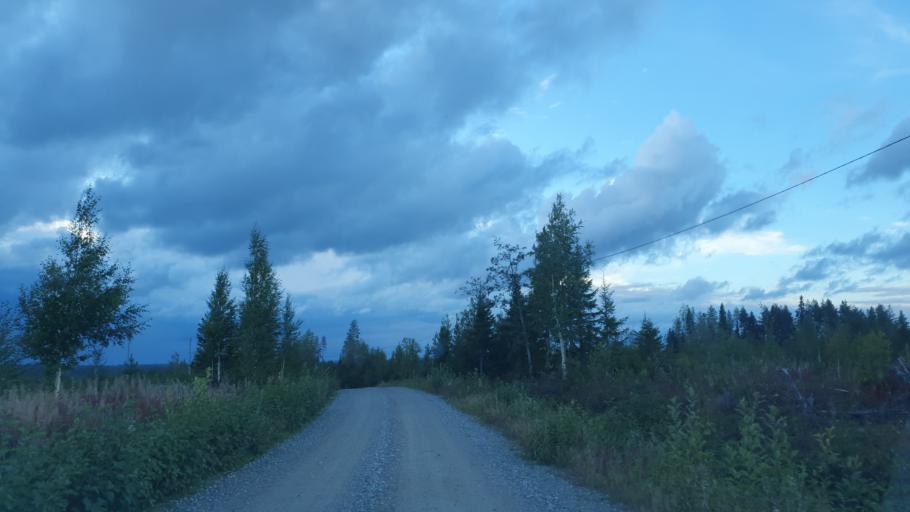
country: FI
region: Kainuu
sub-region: Kehys-Kainuu
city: Kuhmo
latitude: 64.3413
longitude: 29.8814
